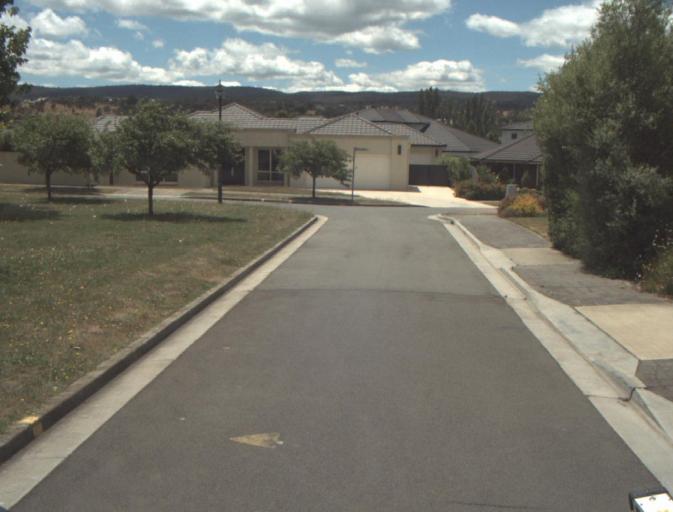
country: AU
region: Tasmania
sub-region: Launceston
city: Newstead
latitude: -41.4363
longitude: 147.1597
